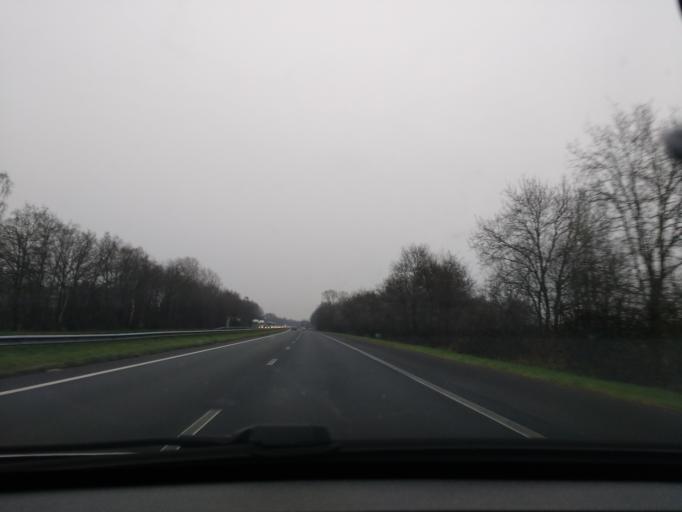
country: NL
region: Gelderland
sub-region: Gemeente Barneveld
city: Barneveld
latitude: 52.1064
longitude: 5.5799
